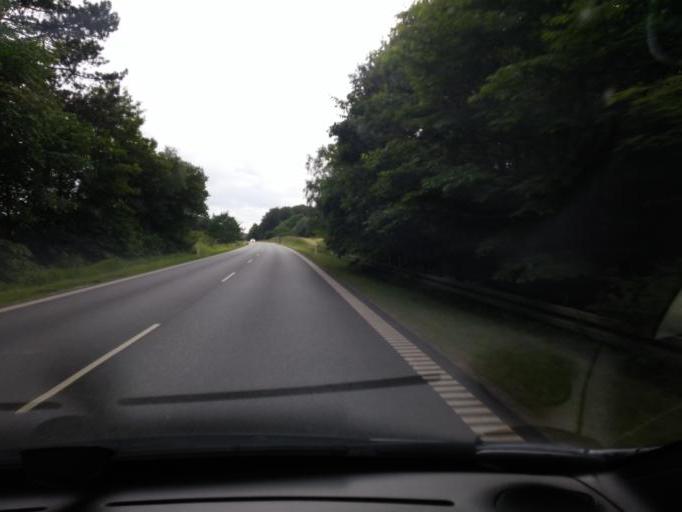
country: DK
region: Capital Region
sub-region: Hillerod Kommune
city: Hillerod
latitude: 55.9548
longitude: 12.2858
